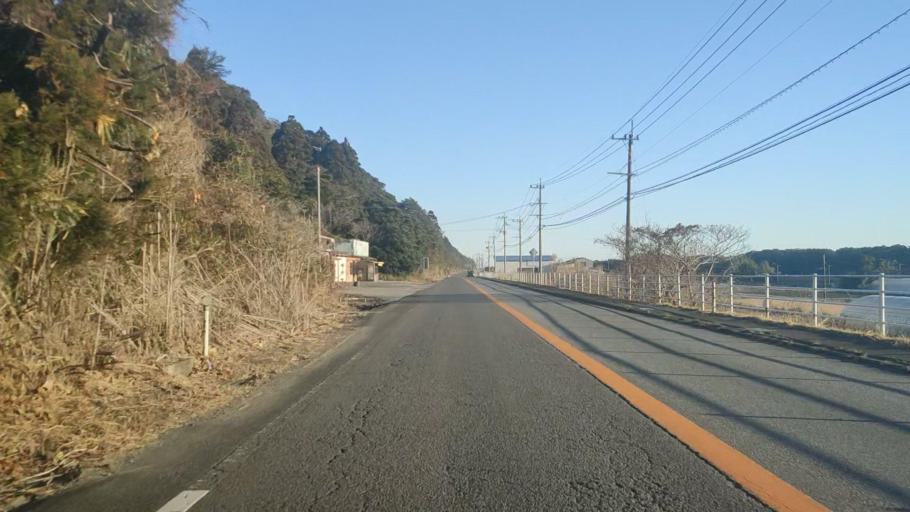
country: JP
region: Miyazaki
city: Takanabe
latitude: 32.0968
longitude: 131.5180
